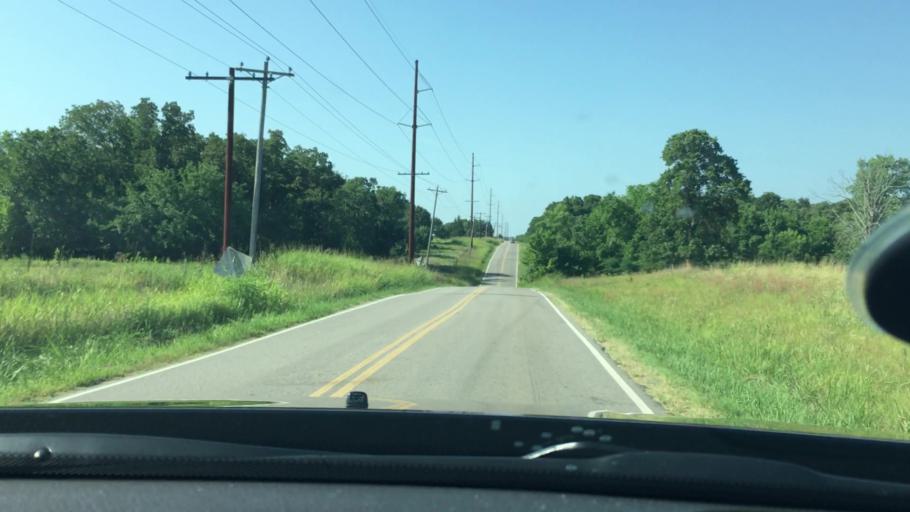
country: US
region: Oklahoma
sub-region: Pontotoc County
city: Ada
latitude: 34.8065
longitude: -96.6348
